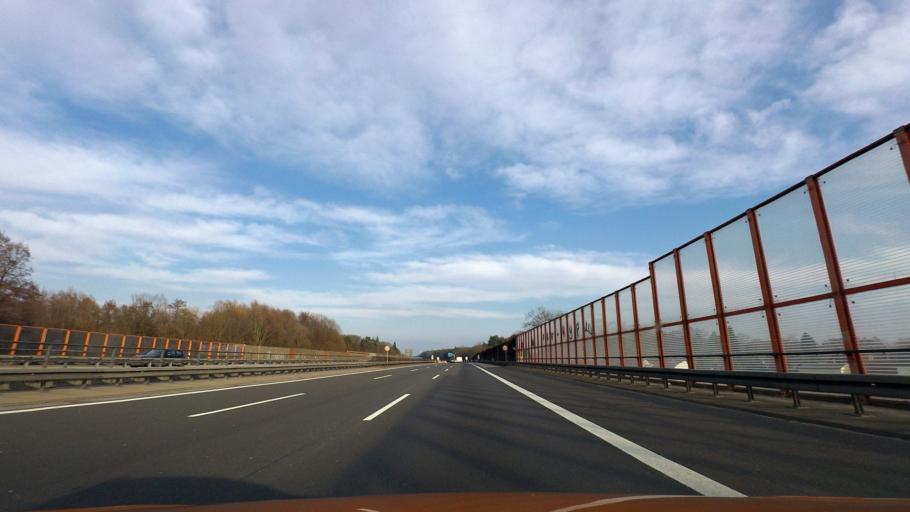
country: DE
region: Brandenburg
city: Gross Kreutz
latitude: 52.3395
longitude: 12.7313
